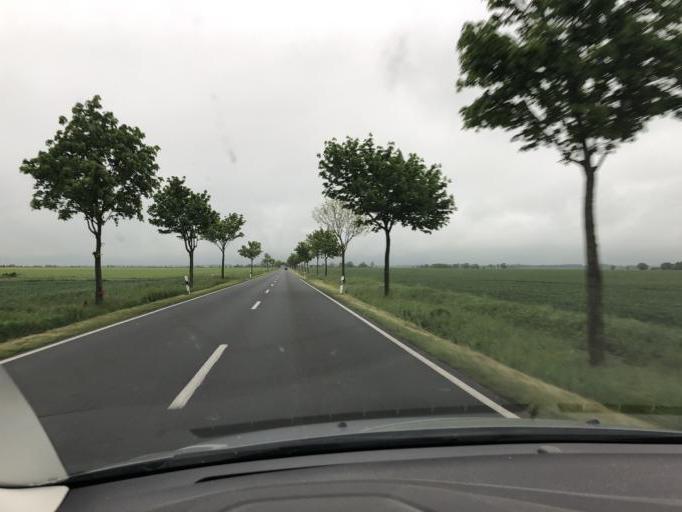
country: DE
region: Saxony
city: Zschortau
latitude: 51.4963
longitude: 12.3963
